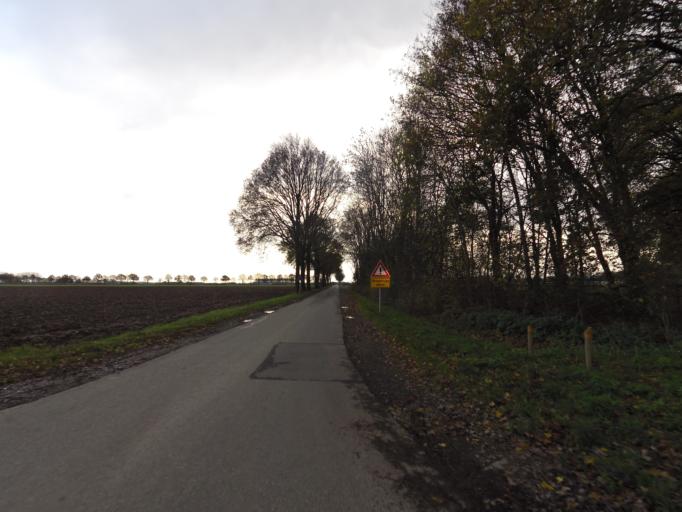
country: NL
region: Gelderland
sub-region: Gemeente Montferland
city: s-Heerenberg
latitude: 51.8836
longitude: 6.2808
